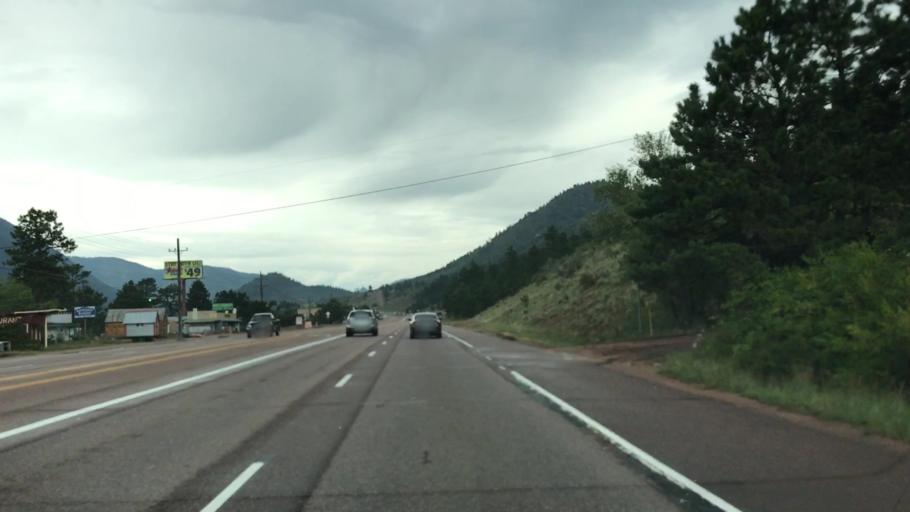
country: US
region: Colorado
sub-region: El Paso County
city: Cascade-Chipita Park
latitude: 38.9141
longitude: -104.9792
